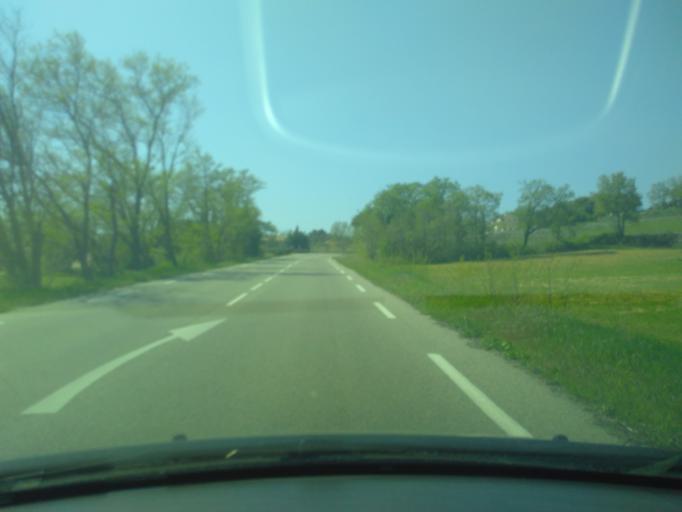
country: FR
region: Rhone-Alpes
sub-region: Departement de la Drome
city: Taulignan
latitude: 44.4334
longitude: 4.9807
